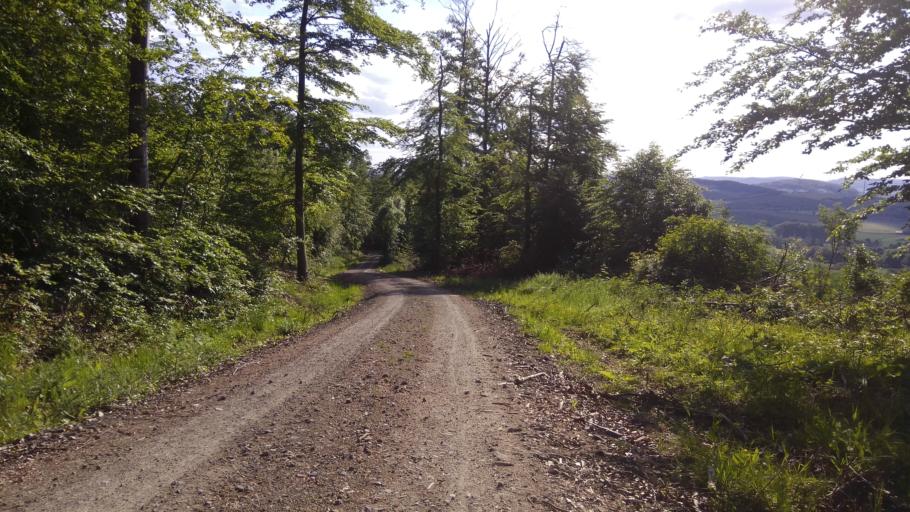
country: DE
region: Lower Saxony
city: Halle
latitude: 52.0027
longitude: 9.5949
